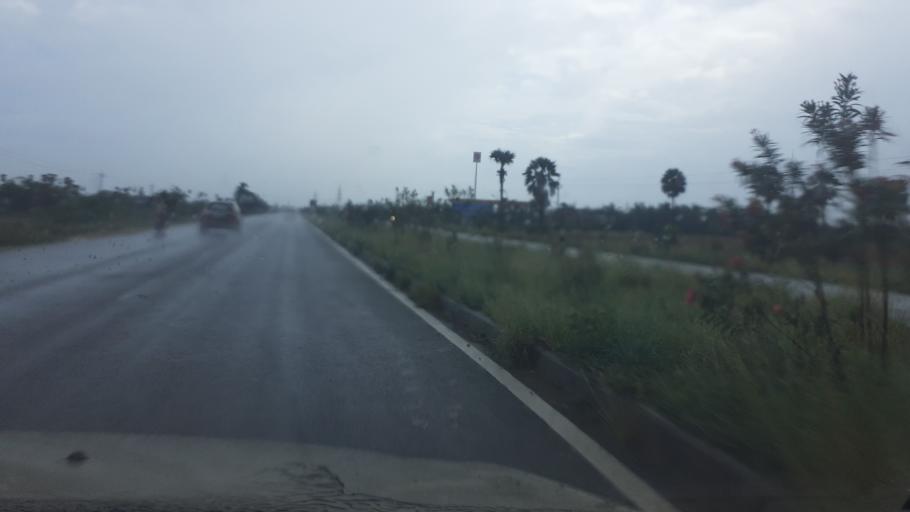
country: IN
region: Tamil Nadu
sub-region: Thoothukkudi
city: Kayattar
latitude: 8.9137
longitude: 77.7649
